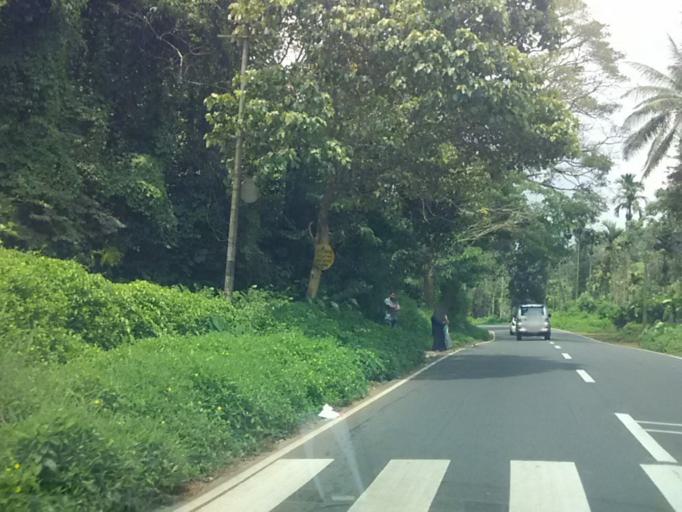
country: IN
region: Kerala
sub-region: Wayanad
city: Kalpetta
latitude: 11.5621
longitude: 76.0421
